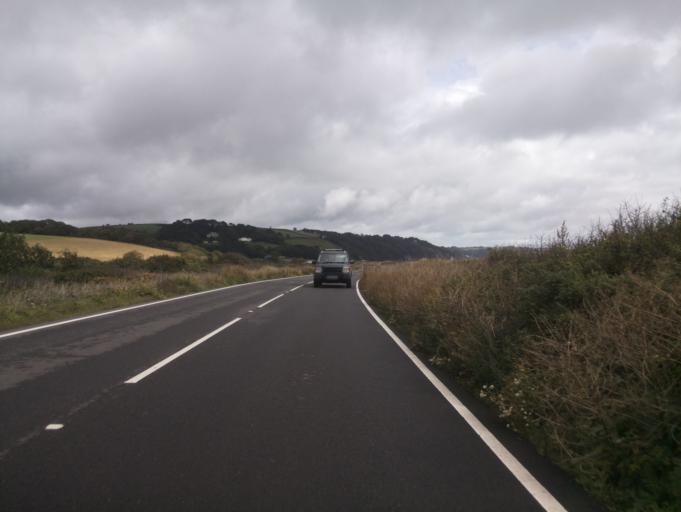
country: GB
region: England
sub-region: Devon
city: Dartmouth
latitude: 50.2906
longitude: -3.6431
